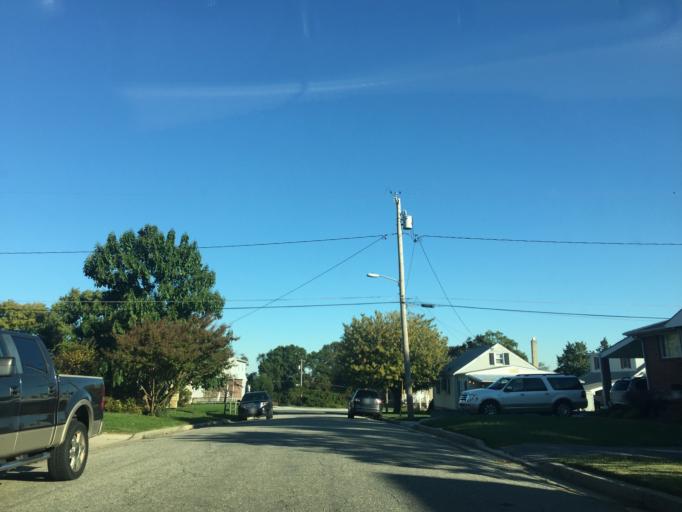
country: US
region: Maryland
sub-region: Baltimore County
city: Dundalk
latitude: 39.2844
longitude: -76.5229
